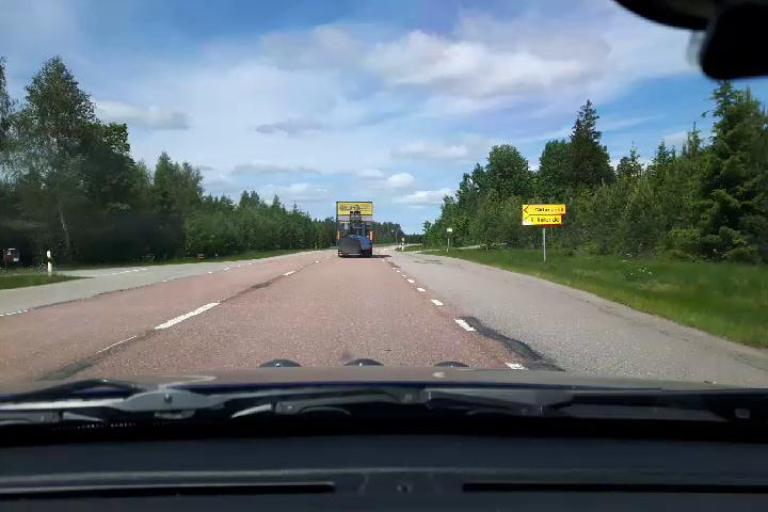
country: SE
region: Uppsala
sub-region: Osthammars Kommun
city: Bjorklinge
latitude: 60.1534
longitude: 17.4919
